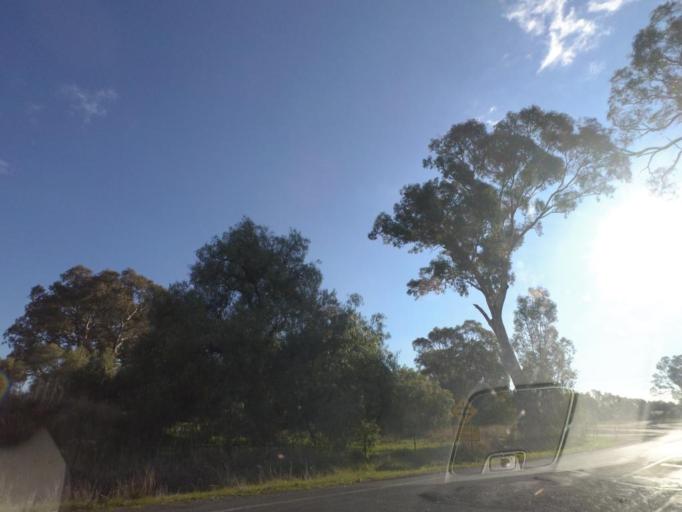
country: AU
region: Victoria
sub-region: Benalla
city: Benalla
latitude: -36.6968
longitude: 145.6584
